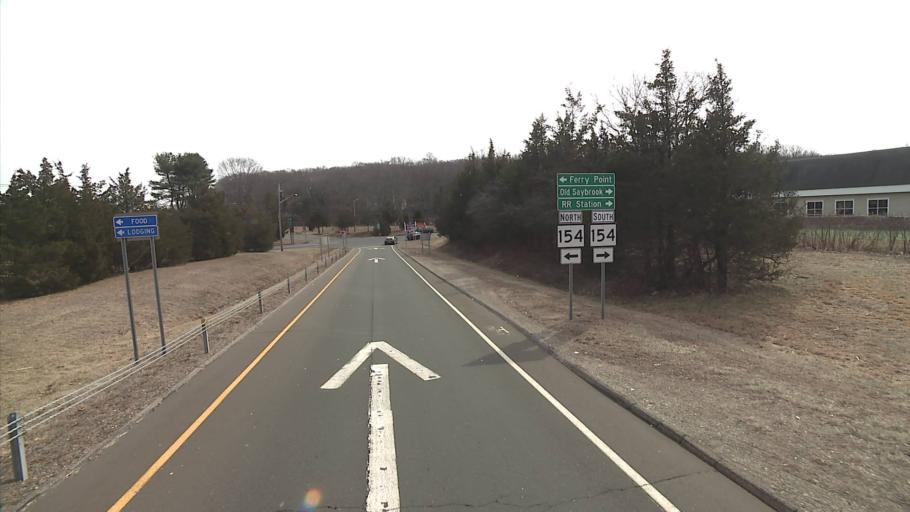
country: US
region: Connecticut
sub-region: Middlesex County
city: Old Saybrook
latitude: 41.3226
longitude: -72.3793
